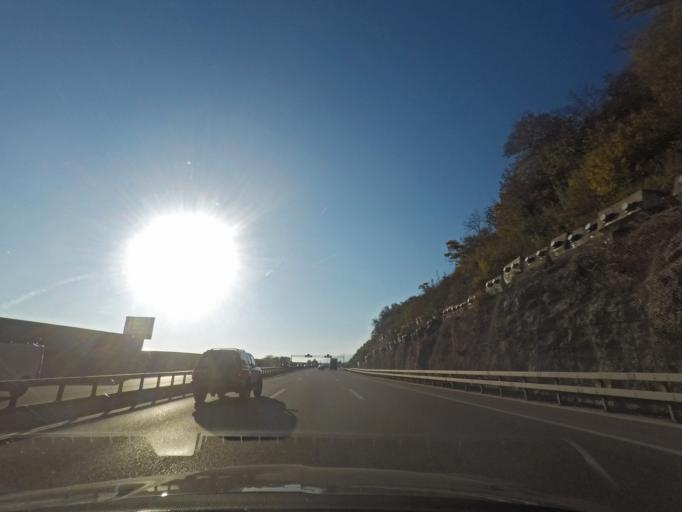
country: CH
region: Aargau
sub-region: Bezirk Zofingen
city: Rothrist
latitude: 47.3124
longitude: 7.8699
